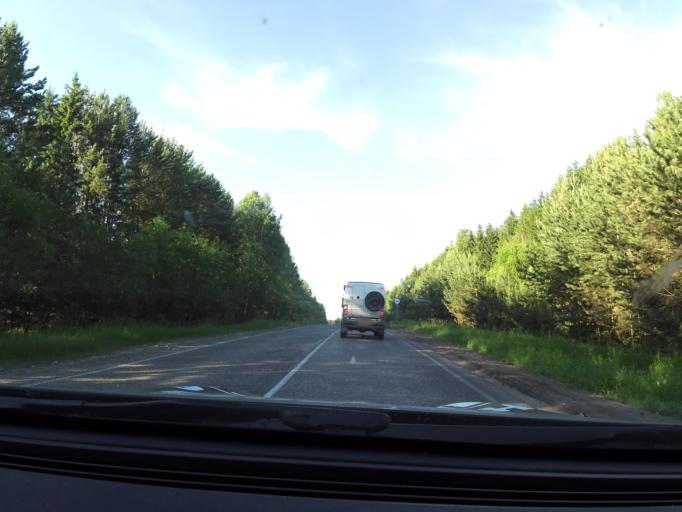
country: RU
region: Kirov
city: Belorechensk
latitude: 58.7914
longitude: 52.3966
